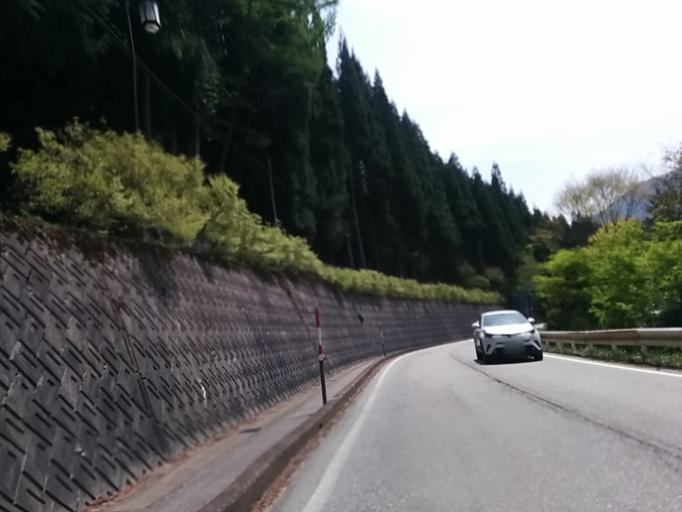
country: JP
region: Gifu
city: Takayama
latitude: 36.2330
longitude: 137.5304
